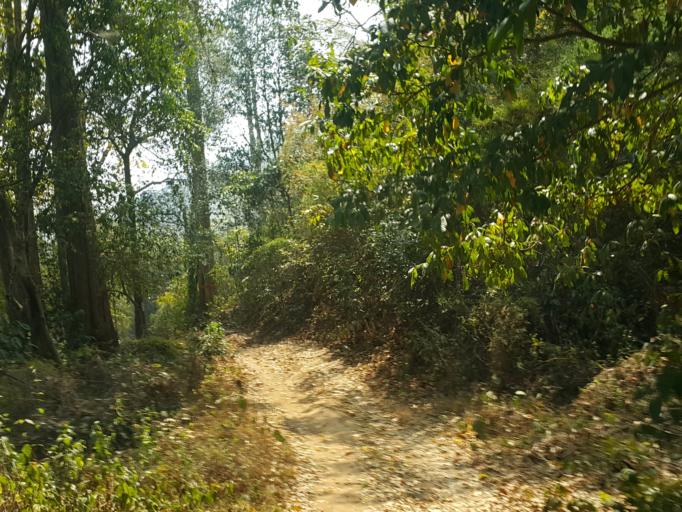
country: TH
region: Chiang Mai
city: Hang Dong
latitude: 18.7512
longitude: 98.8268
